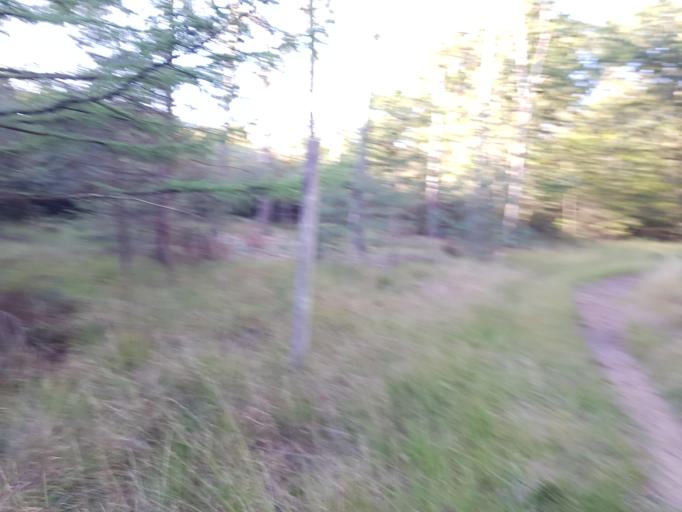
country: NL
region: Gelderland
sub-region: Gemeente Apeldoorn
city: Uddel
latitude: 52.2965
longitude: 5.8146
